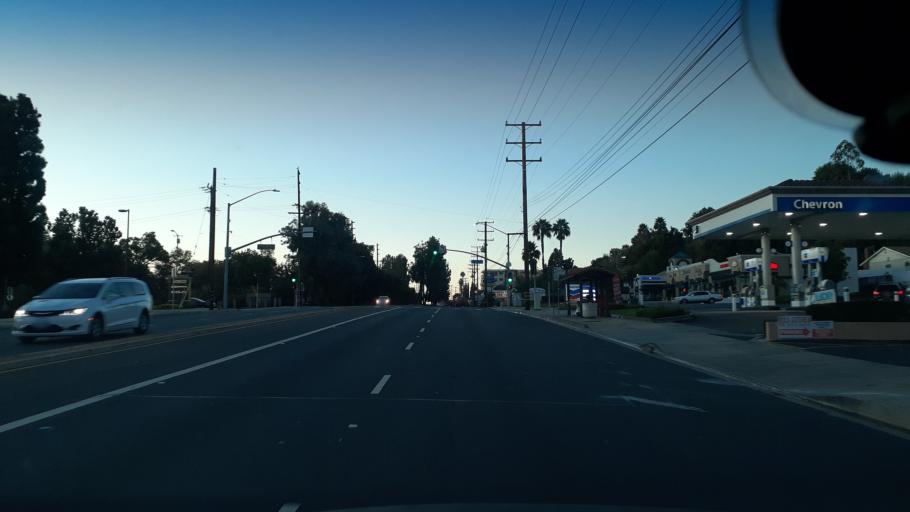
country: US
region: California
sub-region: Los Angeles County
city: San Pedro
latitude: 33.7508
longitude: -118.3092
